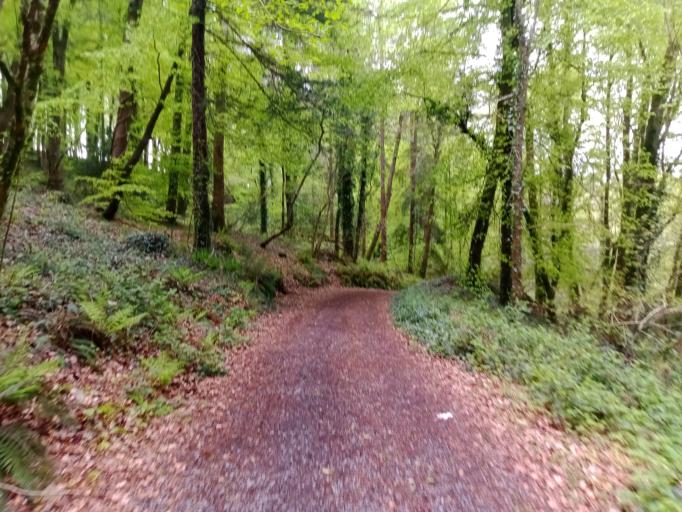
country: IE
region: Leinster
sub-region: Kilkenny
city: Thomastown
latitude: 52.4820
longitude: -7.0649
